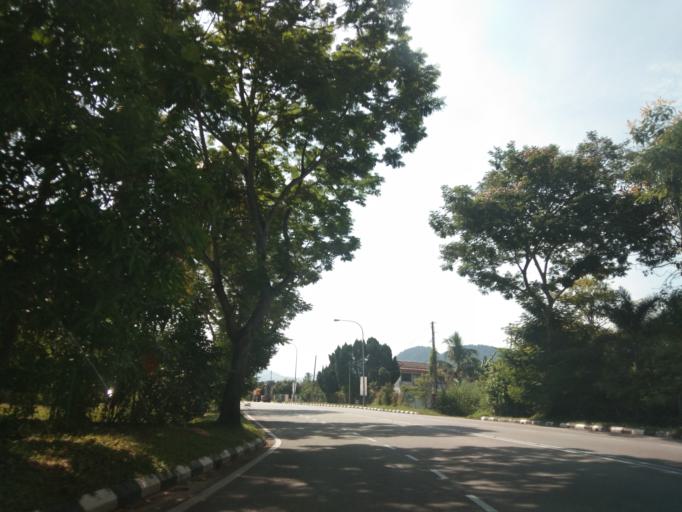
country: MY
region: Perak
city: Ipoh
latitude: 4.5676
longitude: 101.1209
